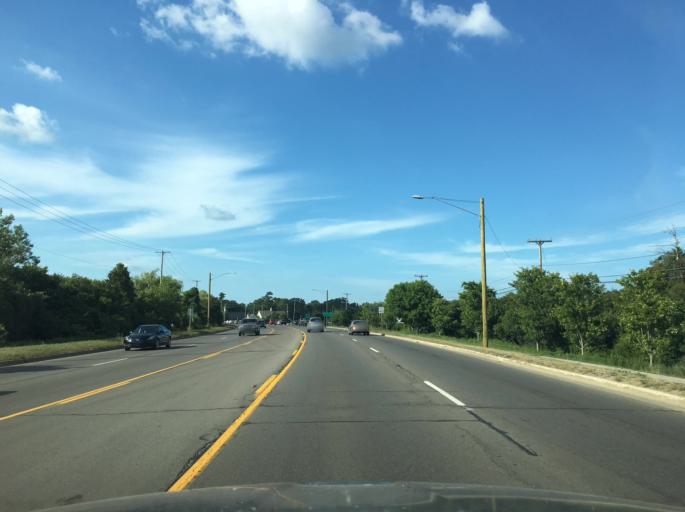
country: US
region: Michigan
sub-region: Grand Traverse County
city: Traverse City
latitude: 44.7483
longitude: -85.6360
